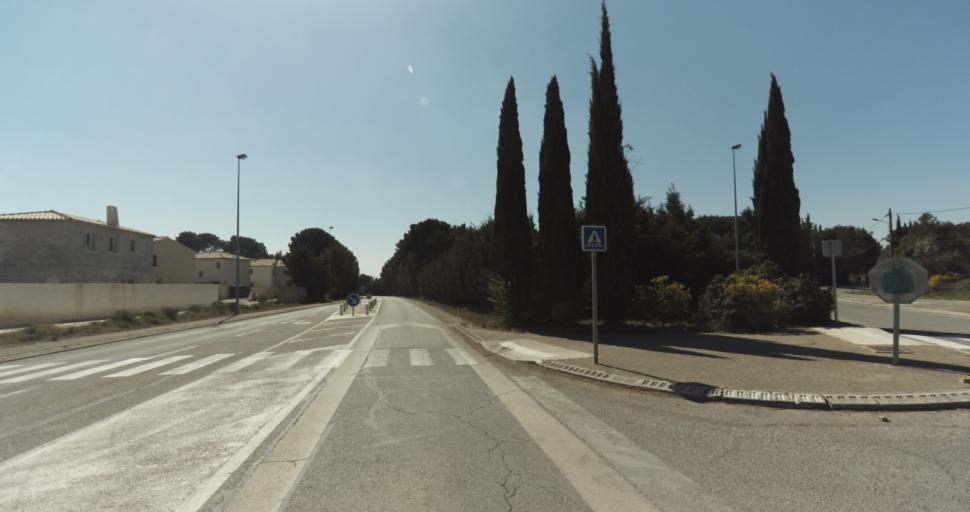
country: FR
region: Provence-Alpes-Cote d'Azur
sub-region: Departement des Bouches-du-Rhone
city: Pelissanne
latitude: 43.6341
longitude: 5.1678
